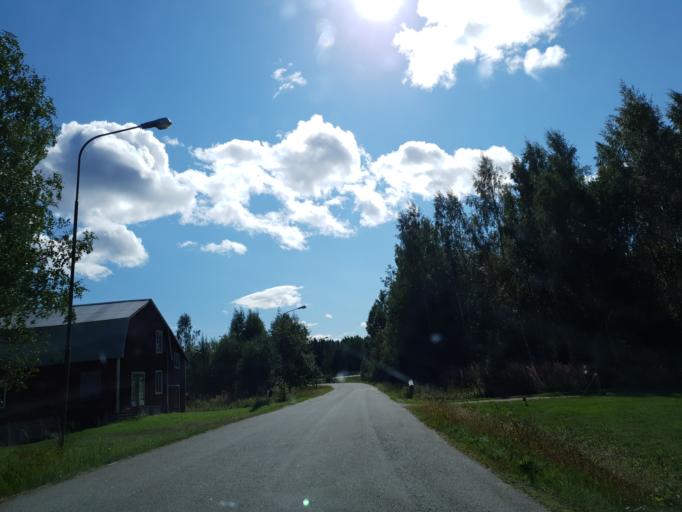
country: SE
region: Vaesternorrland
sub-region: OErnskoeldsviks Kommun
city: Husum
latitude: 63.3434
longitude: 19.1136
